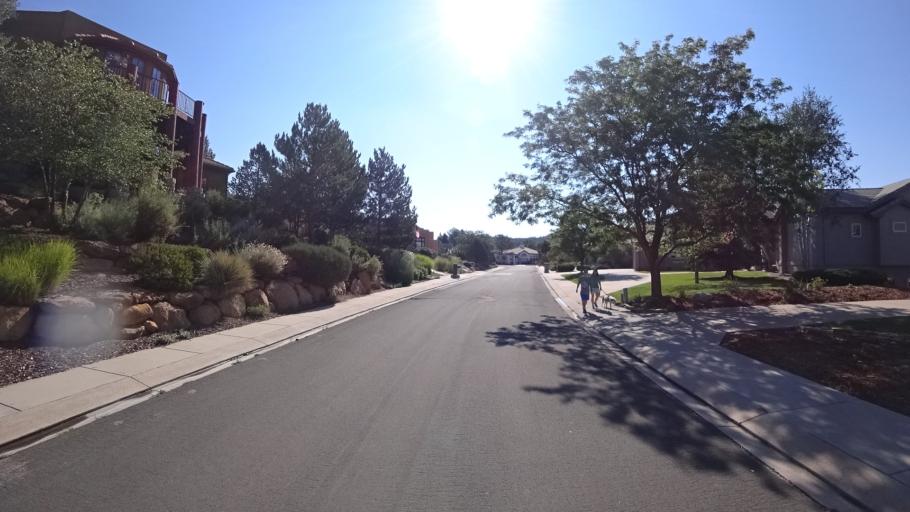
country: US
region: Colorado
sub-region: El Paso County
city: Colorado Springs
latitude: 38.8791
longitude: -104.7873
